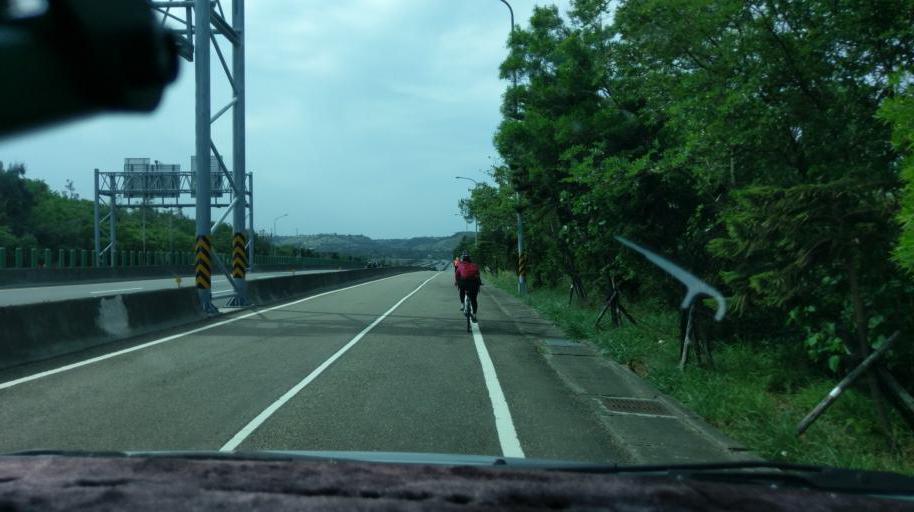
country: TW
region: Taiwan
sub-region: Miaoli
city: Miaoli
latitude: 24.6090
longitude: 120.7512
